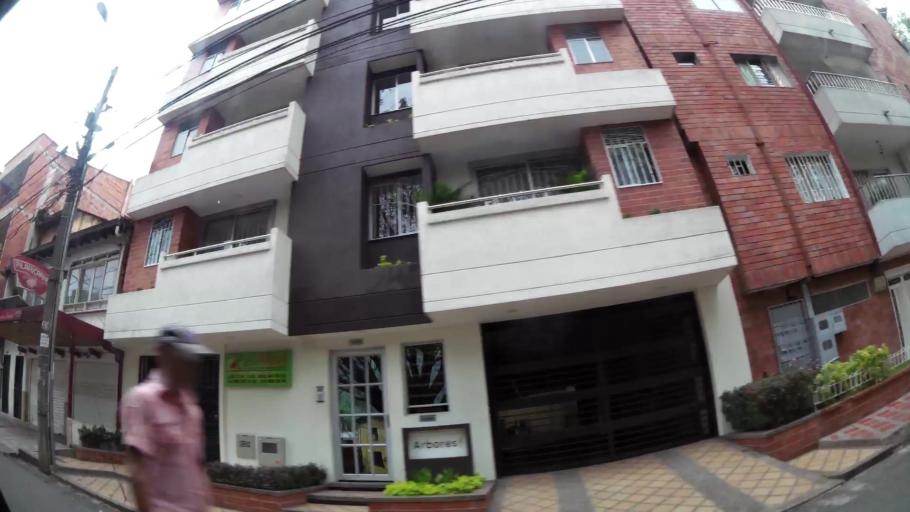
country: CO
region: Antioquia
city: Medellin
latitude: 6.2736
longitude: -75.5804
